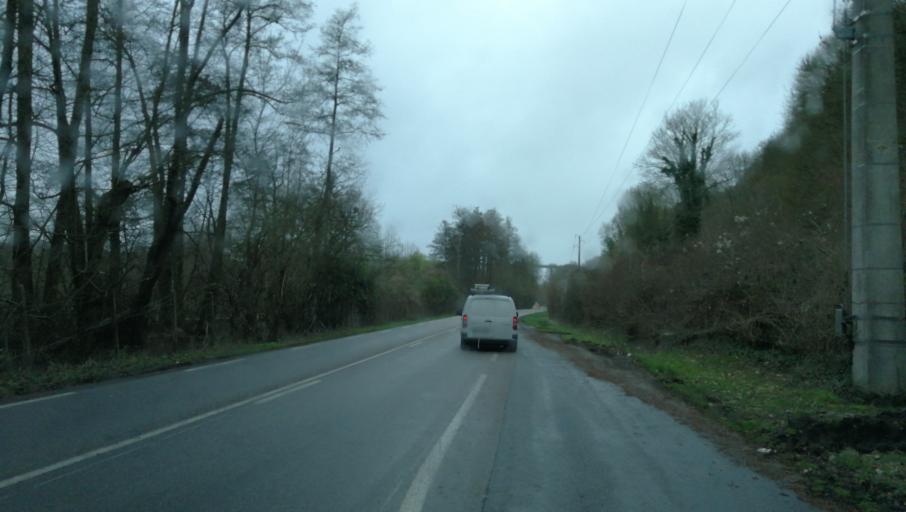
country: FR
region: Haute-Normandie
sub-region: Departement de l'Eure
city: Nassandres
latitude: 49.1545
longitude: 0.7292
